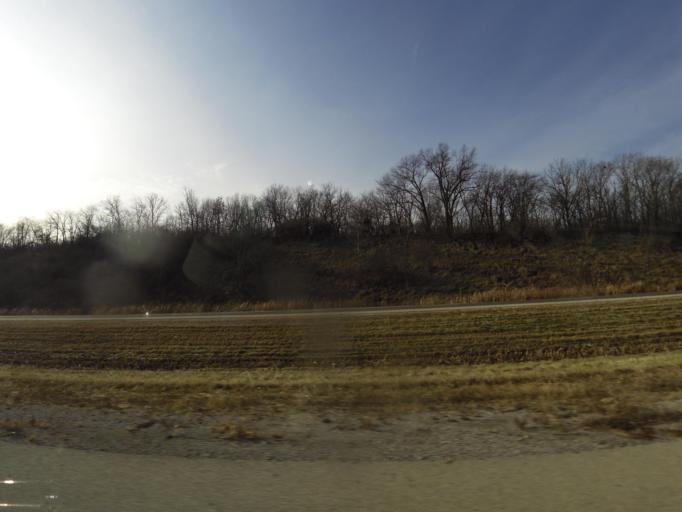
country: US
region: Illinois
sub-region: Macon County
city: Harristown
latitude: 39.8177
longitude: -89.0317
